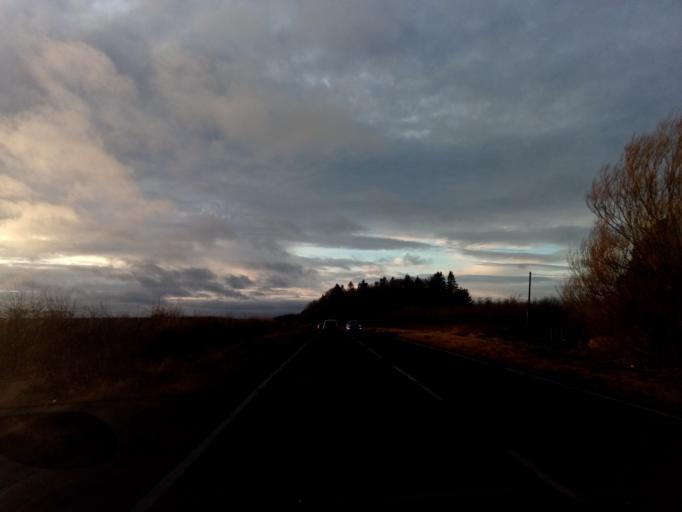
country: GB
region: England
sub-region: Northumberland
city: Stannington
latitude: 55.0792
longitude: -1.6516
